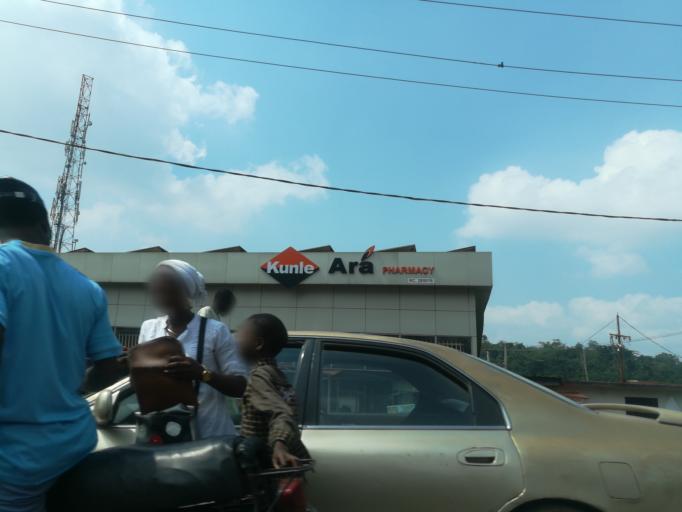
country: NG
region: Oyo
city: Ibadan
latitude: 7.4005
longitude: 3.8990
